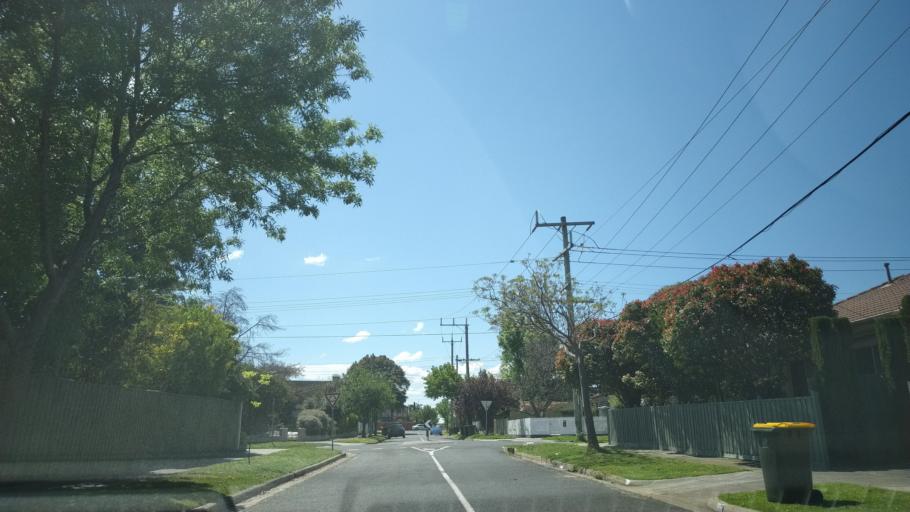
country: AU
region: Victoria
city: Murrumbeena
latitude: -37.9076
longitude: 145.0580
